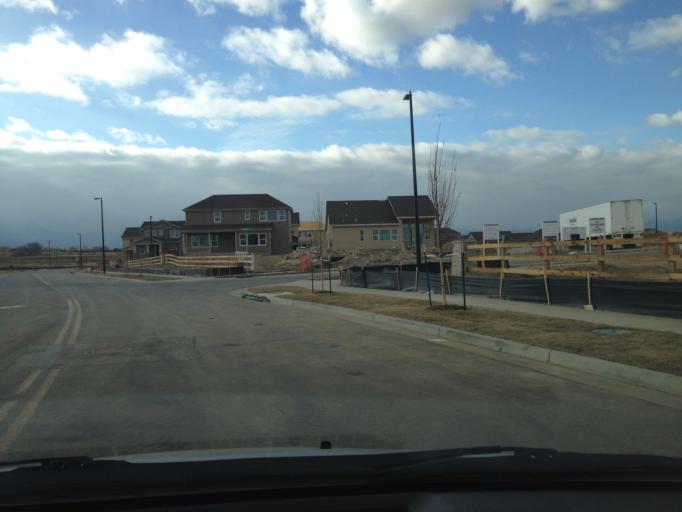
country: US
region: Colorado
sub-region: Boulder County
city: Lafayette
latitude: 40.0260
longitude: -105.0842
